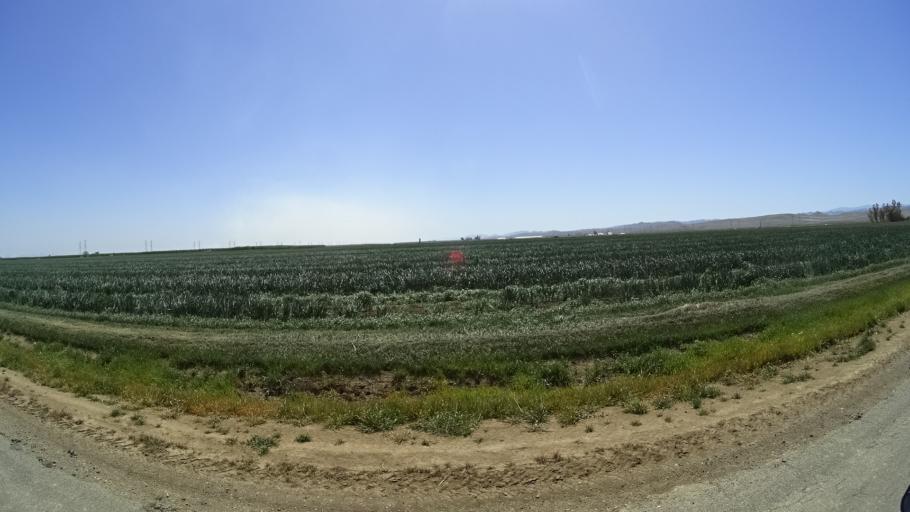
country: US
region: California
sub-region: Glenn County
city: Willows
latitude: 39.4656
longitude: -122.2713
